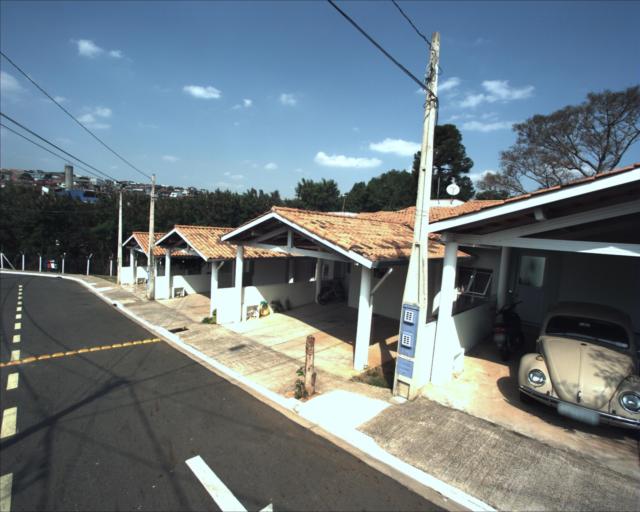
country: BR
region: Sao Paulo
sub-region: Sorocaba
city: Sorocaba
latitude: -23.4522
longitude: -47.4944
